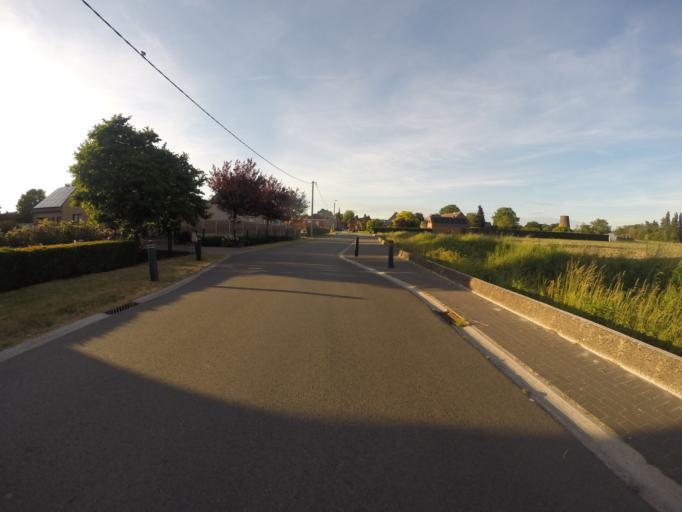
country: BE
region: Flanders
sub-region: Provincie Oost-Vlaanderen
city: Aalter
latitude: 51.1254
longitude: 3.4845
